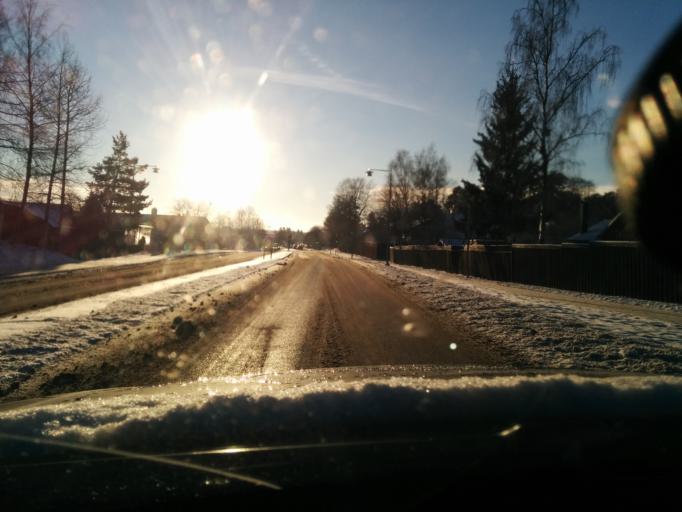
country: SE
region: Stockholm
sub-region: Vallentuna Kommun
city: Vallentuna
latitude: 59.4964
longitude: 18.0619
